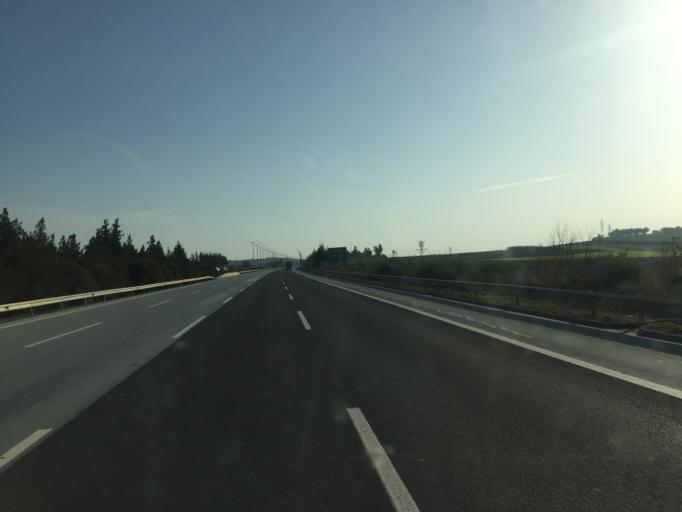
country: TR
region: Mersin
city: Yenice
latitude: 37.0231
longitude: 35.0531
